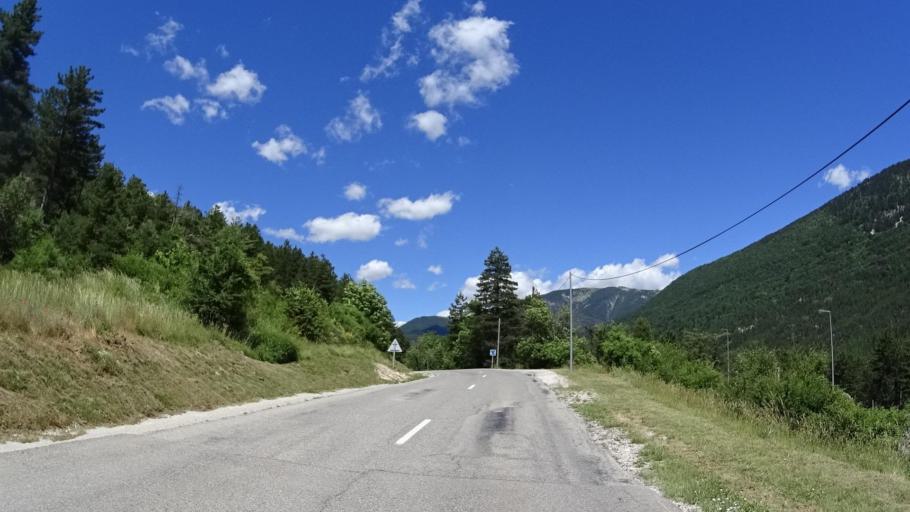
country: FR
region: Provence-Alpes-Cote d'Azur
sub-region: Departement des Alpes-de-Haute-Provence
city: Annot
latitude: 43.9872
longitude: 6.5331
